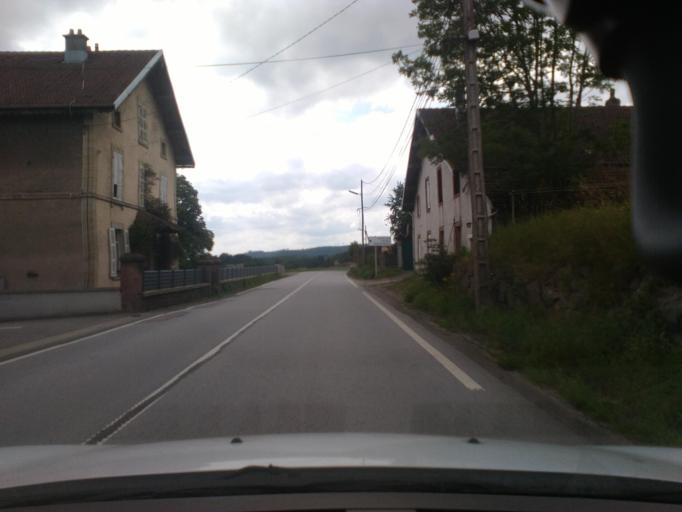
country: FR
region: Lorraine
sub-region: Departement des Vosges
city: Docelles
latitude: 48.1686
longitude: 6.6592
